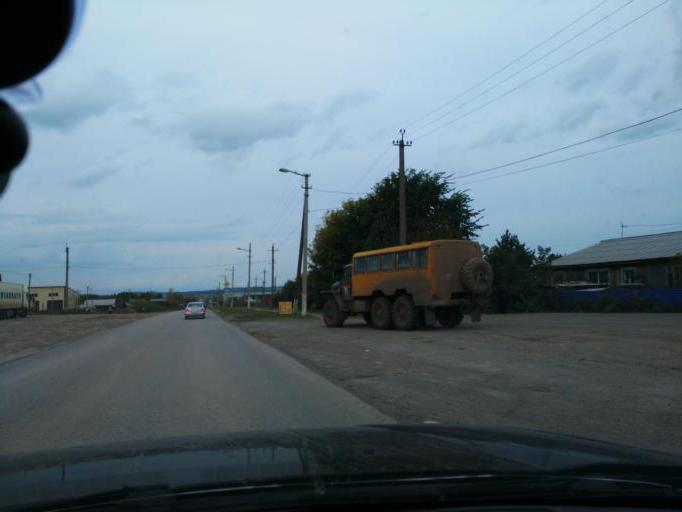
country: RU
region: Perm
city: Chernushka
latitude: 56.5345
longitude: 56.0971
